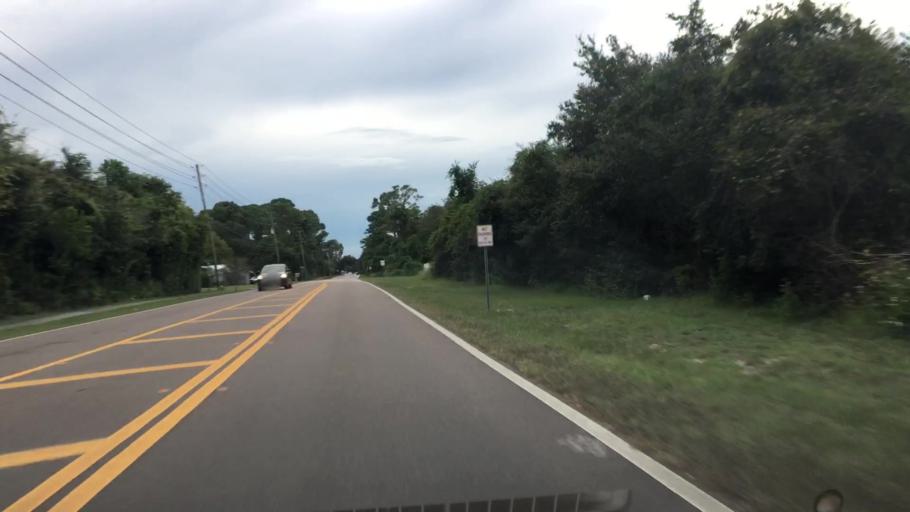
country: US
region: Florida
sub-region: Volusia County
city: DeBary
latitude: 28.8903
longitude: -81.2936
